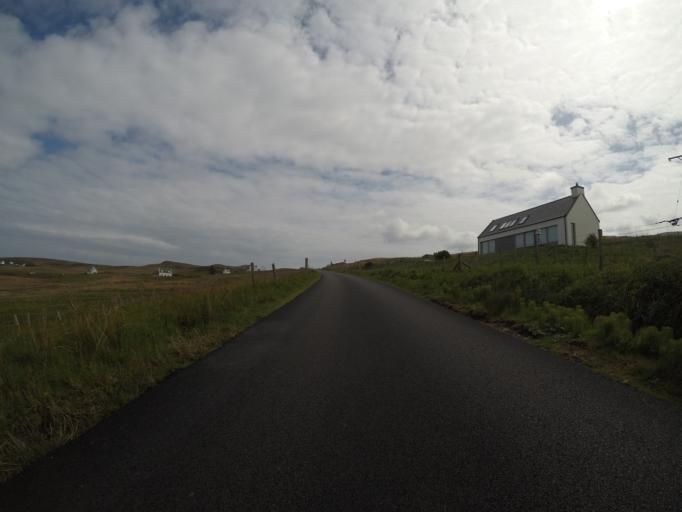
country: GB
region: Scotland
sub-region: Highland
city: Portree
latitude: 57.6827
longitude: -6.2987
